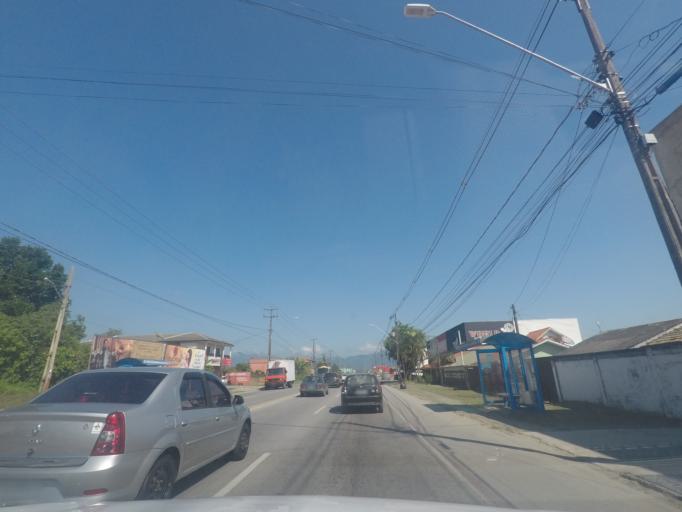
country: BR
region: Parana
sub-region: Paranagua
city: Paranagua
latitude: -25.5602
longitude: -48.5611
